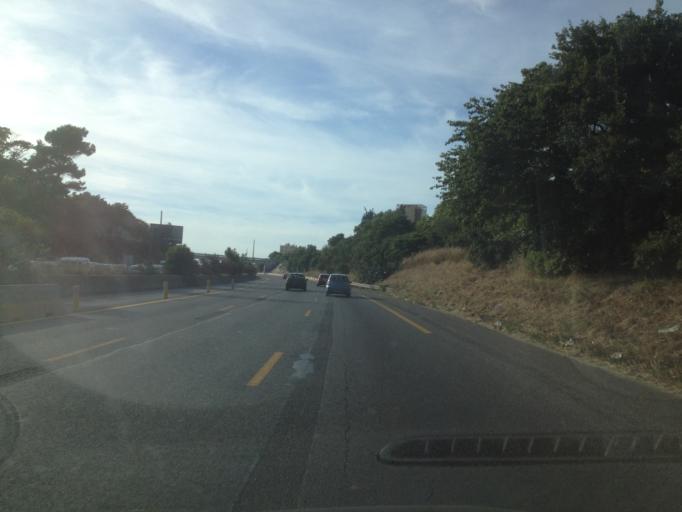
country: FR
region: Provence-Alpes-Cote d'Azur
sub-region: Departement des Bouches-du-Rhone
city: Marseille 14
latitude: 43.3438
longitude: 5.3755
